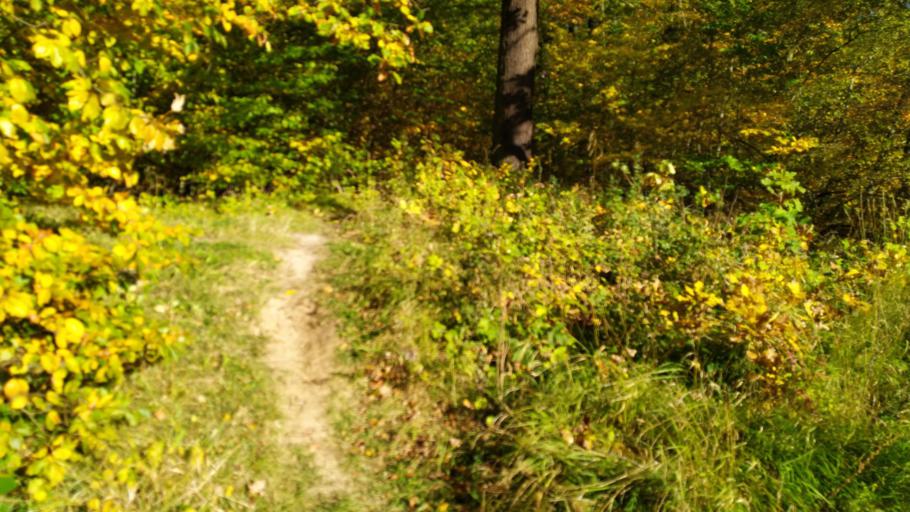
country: DE
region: Thuringia
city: Kleinobringen
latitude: 51.0147
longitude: 11.3233
